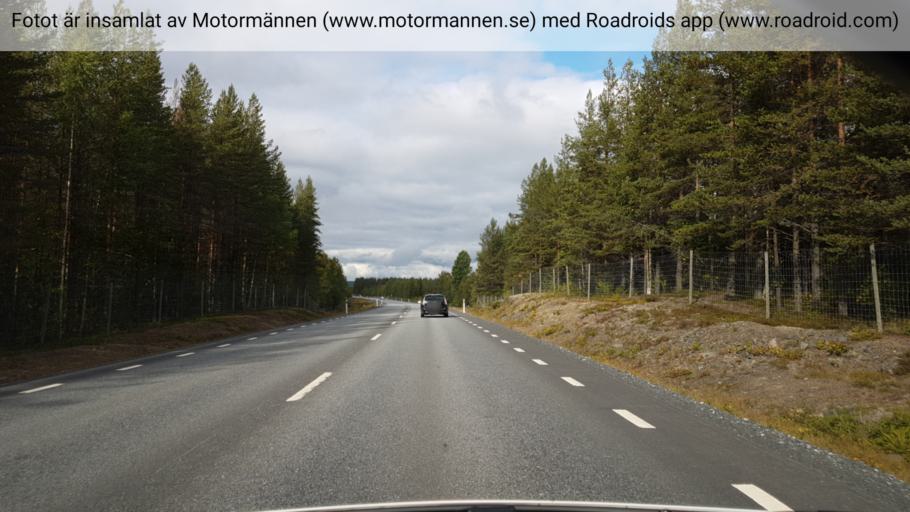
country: SE
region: Vaesterbotten
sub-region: Skelleftea Kommun
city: Forsbacka
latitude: 64.8253
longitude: 20.5825
